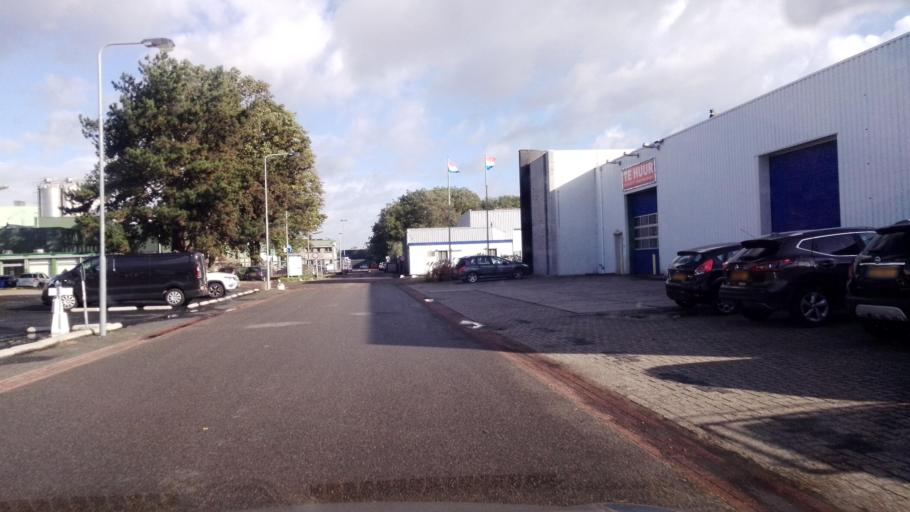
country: NL
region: Limburg
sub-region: Gemeente Venlo
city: Arcen
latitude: 51.4458
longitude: 6.1795
